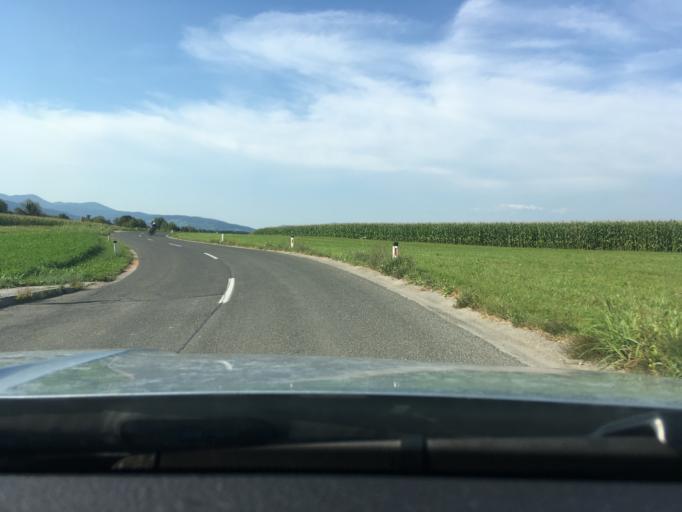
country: SI
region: Crnomelj
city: Crnomelj
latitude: 45.5302
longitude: 15.1632
